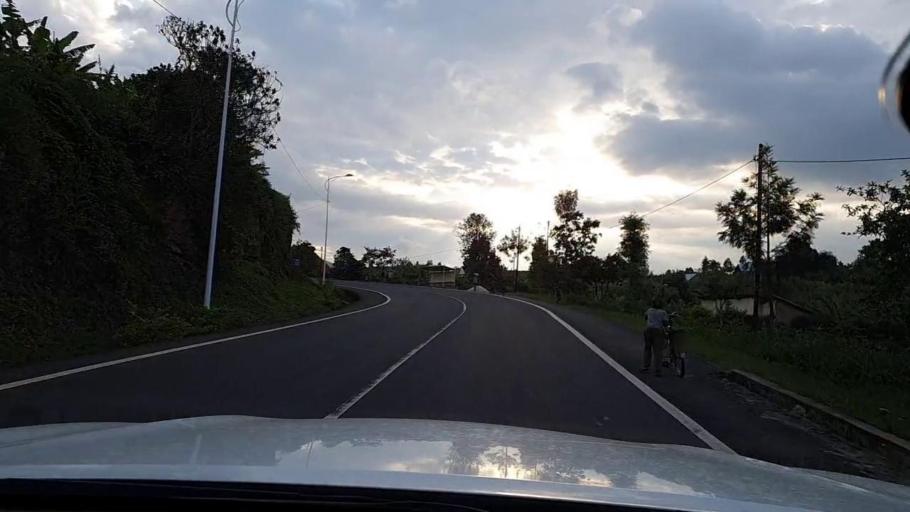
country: RW
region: Western Province
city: Kibuye
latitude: -2.0863
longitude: 29.4149
